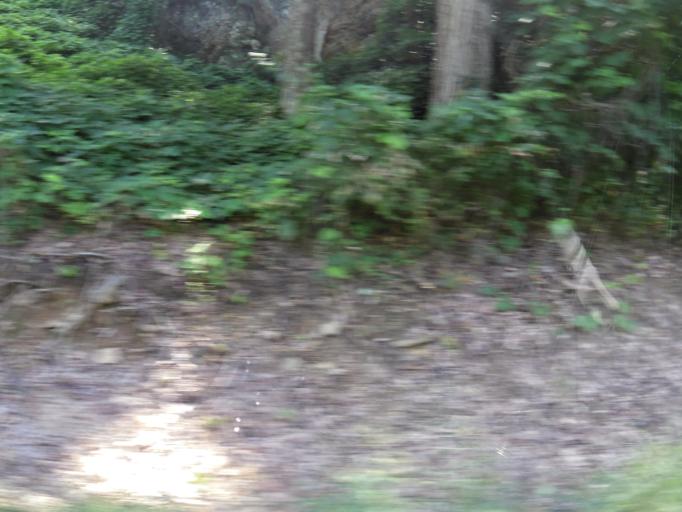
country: US
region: Kentucky
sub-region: Harlan County
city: Harlan
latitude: 36.8907
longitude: -83.3140
